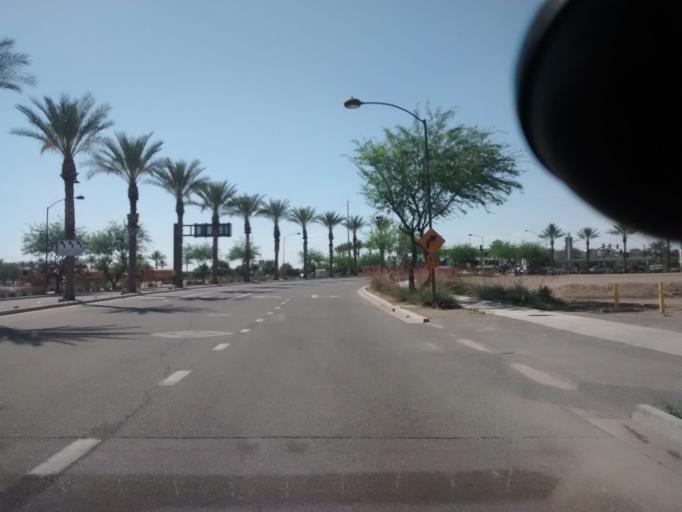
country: US
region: Arizona
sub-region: Maricopa County
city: Peoria
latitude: 33.5361
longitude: -112.2582
